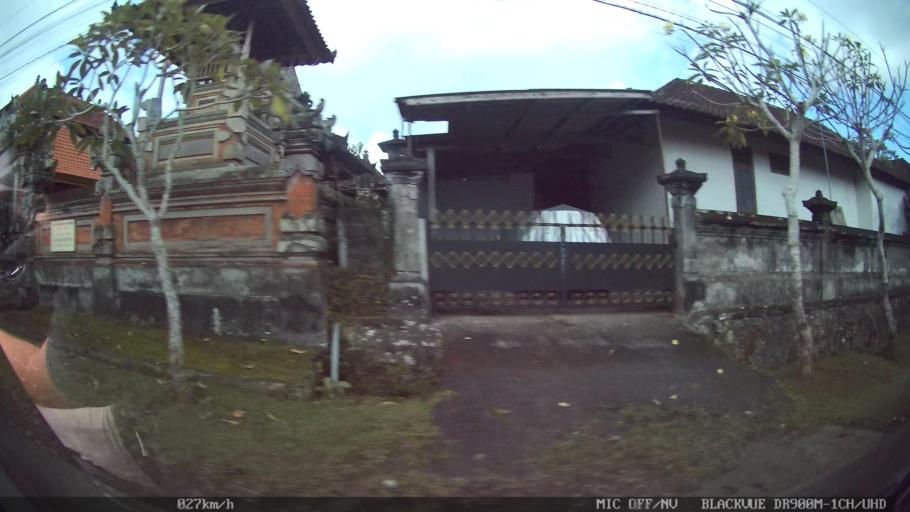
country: ID
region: Bali
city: Banjar Pesalakan
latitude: -8.5035
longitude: 115.3038
